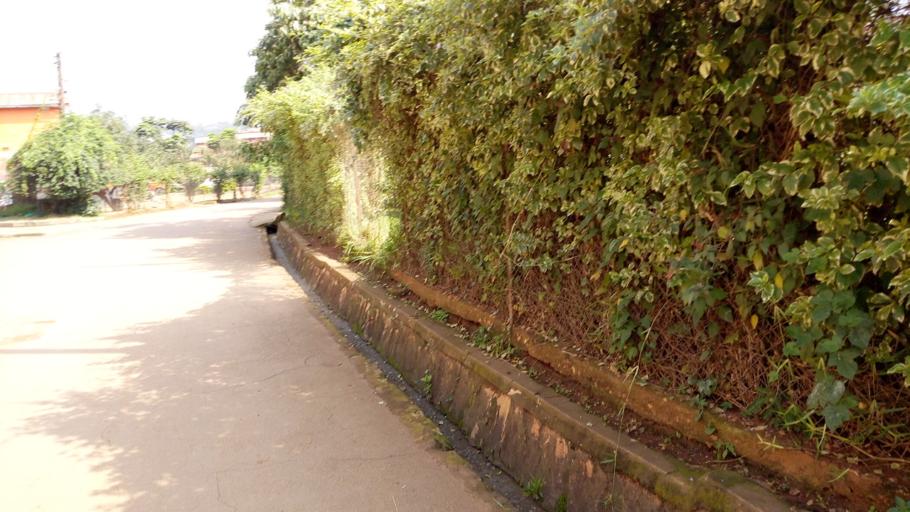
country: UG
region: Central Region
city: Kampala Central Division
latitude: 0.3332
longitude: 32.5669
